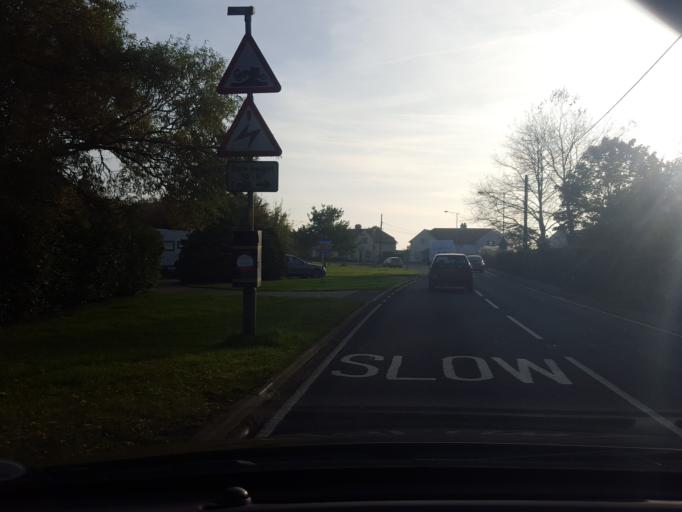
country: GB
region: England
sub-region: Essex
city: Frinton-on-Sea
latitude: 51.8329
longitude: 1.2099
